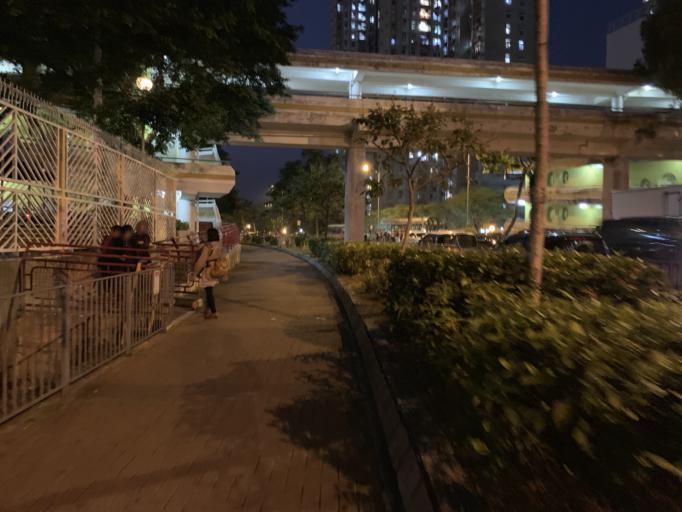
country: HK
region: Tsuen Wan
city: Tsuen Wan
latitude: 22.3620
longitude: 114.1020
